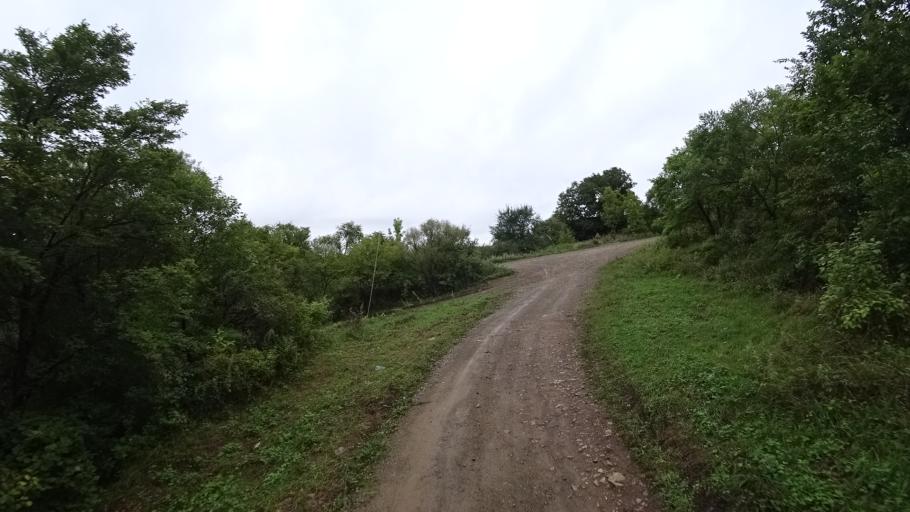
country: RU
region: Primorskiy
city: Monastyrishche
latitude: 44.2754
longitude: 132.4055
